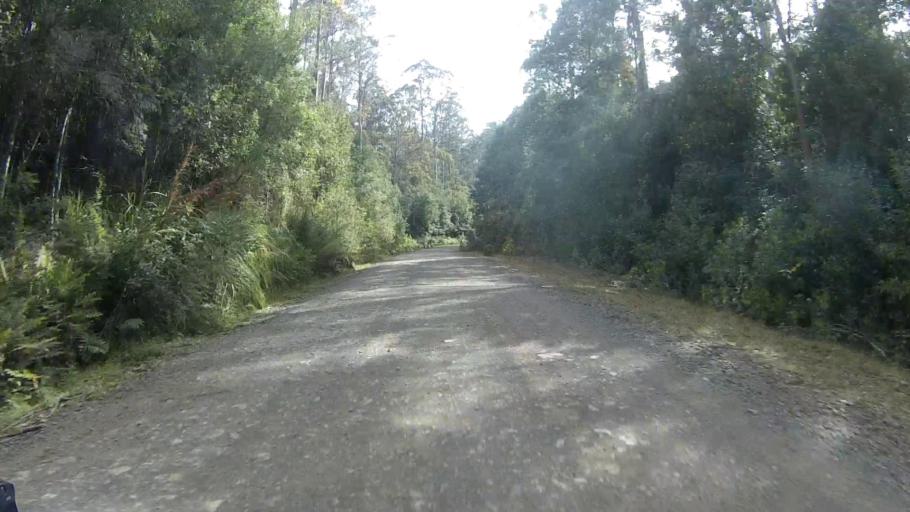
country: AU
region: Tasmania
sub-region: Sorell
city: Sorell
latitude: -42.7400
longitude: 147.8296
